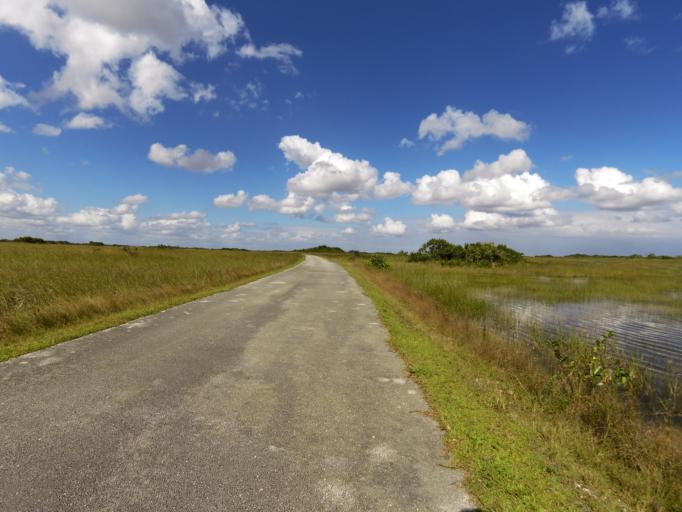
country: US
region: Florida
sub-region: Miami-Dade County
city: The Hammocks
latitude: 25.6909
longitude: -80.7595
